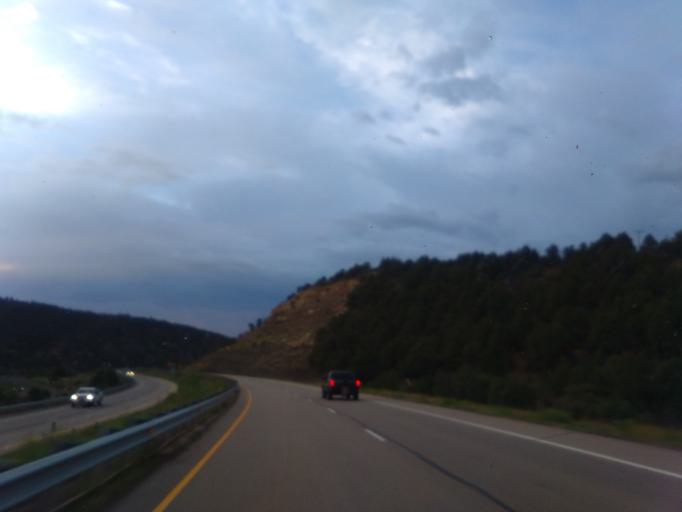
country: US
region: Colorado
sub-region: Las Animas County
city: Trinidad
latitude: 37.0822
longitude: -104.5193
